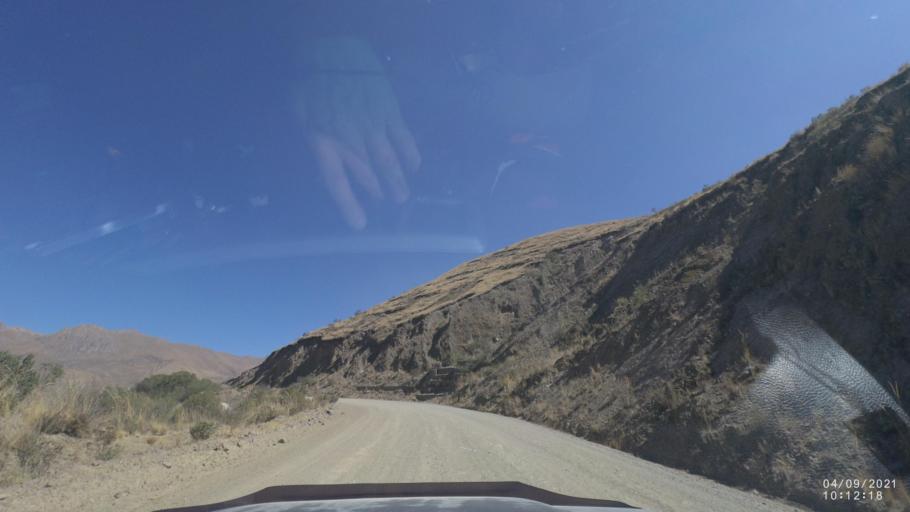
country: BO
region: Cochabamba
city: Sipe Sipe
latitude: -17.3414
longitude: -66.3990
